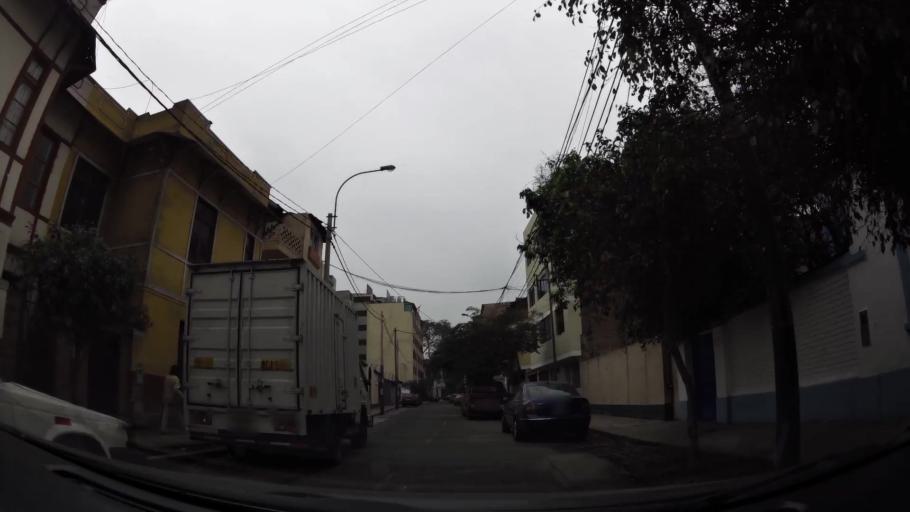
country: PE
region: Lima
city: Lima
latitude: -12.0724
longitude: -77.0316
